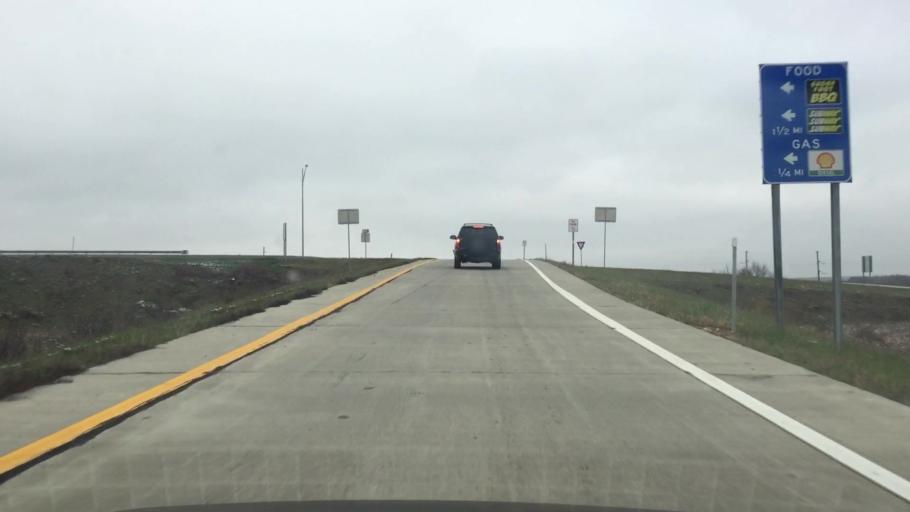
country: US
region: Missouri
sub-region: Saint Clair County
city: Osceola
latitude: 38.0398
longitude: -93.6802
